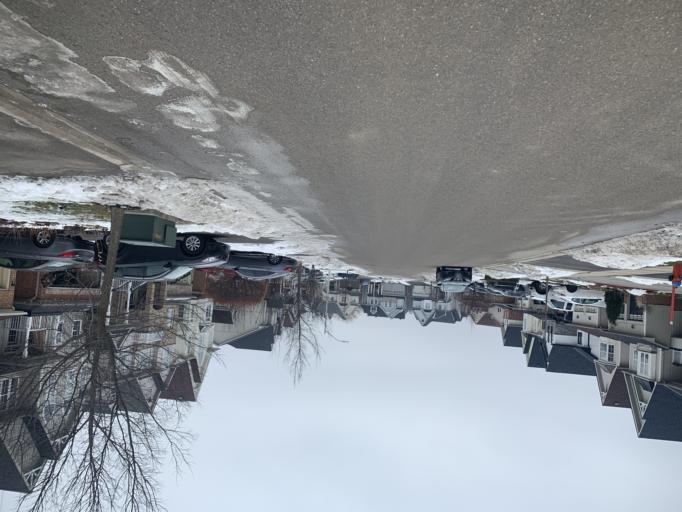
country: CA
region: Ontario
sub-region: Halton
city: Milton
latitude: 43.6599
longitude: -79.9232
